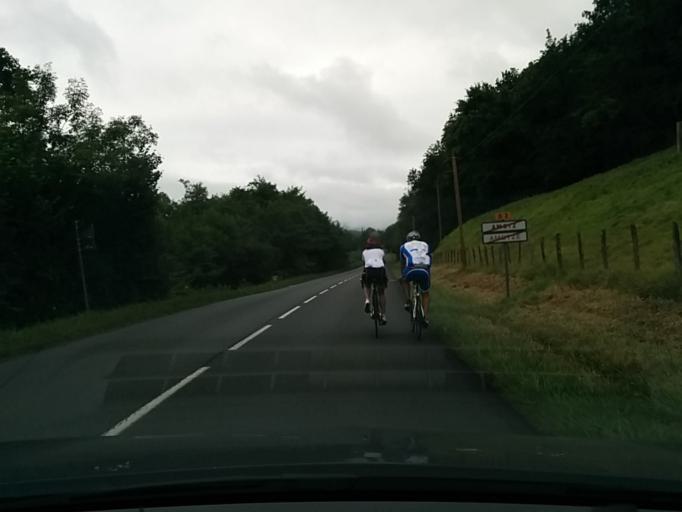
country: FR
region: Aquitaine
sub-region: Departement des Pyrenees-Atlantiques
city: Saint-Pee-sur-Nivelle
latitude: 43.3285
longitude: -1.5452
